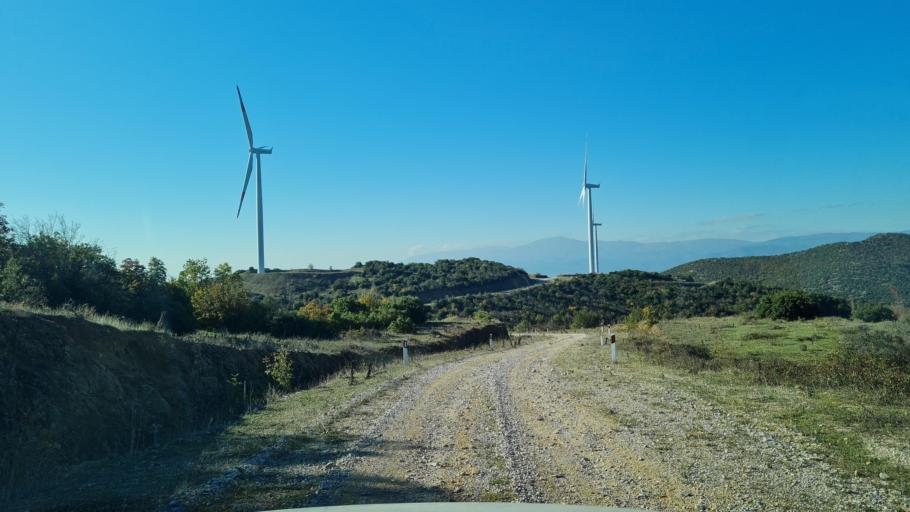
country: MK
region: Bogdanci
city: Bogdanci
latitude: 41.2201
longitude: 22.5477
